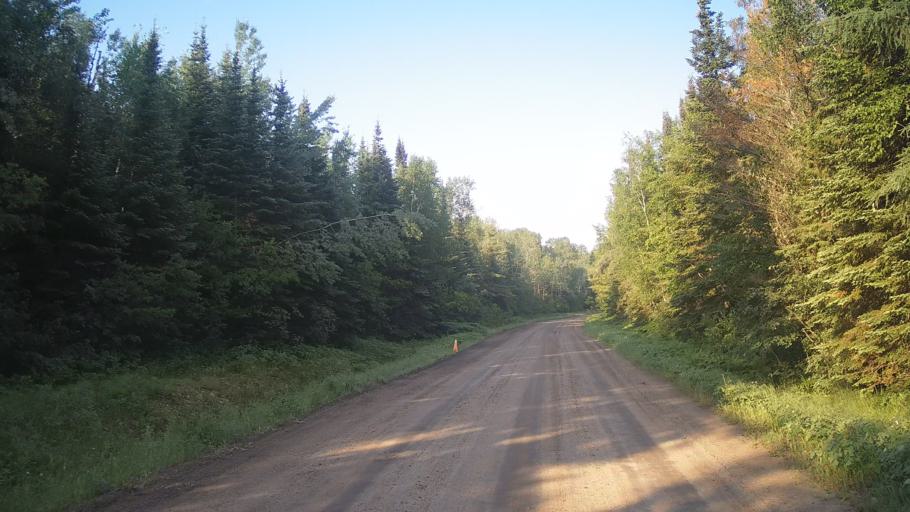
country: CA
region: Ontario
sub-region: Rainy River District
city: Atikokan
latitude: 49.3999
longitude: -91.6623
